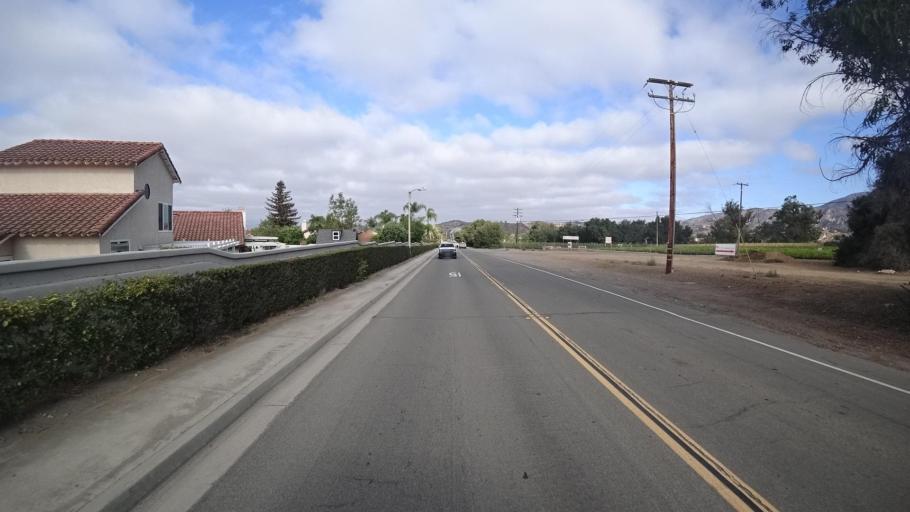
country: US
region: California
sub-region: Orange County
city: Trabuco Canyon
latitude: 33.6576
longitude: -117.5779
